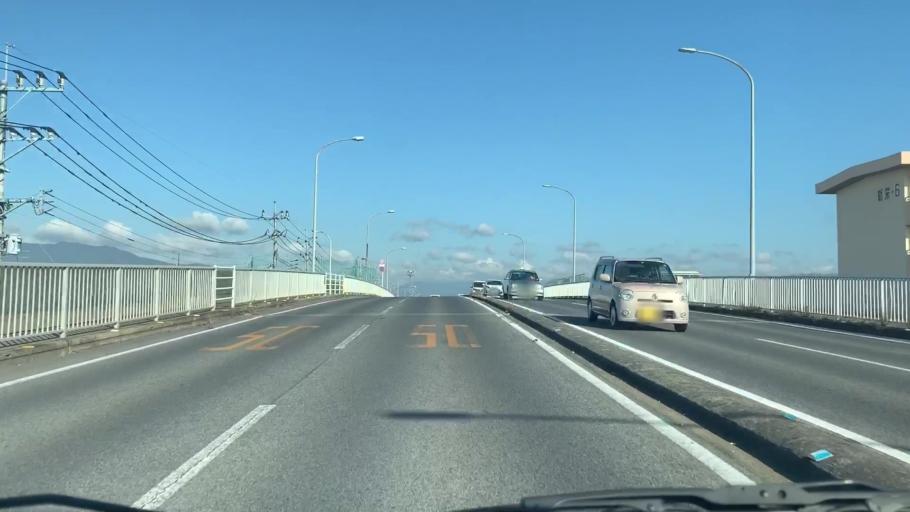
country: JP
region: Saga Prefecture
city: Saga-shi
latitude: 33.2588
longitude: 130.2732
